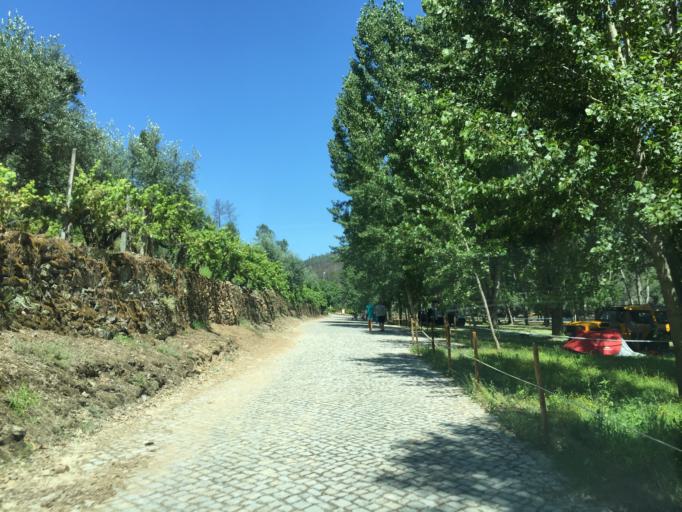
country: PT
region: Coimbra
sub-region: Pampilhosa da Serra
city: Pampilhosa da Serra
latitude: 40.0117
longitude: -7.8461
